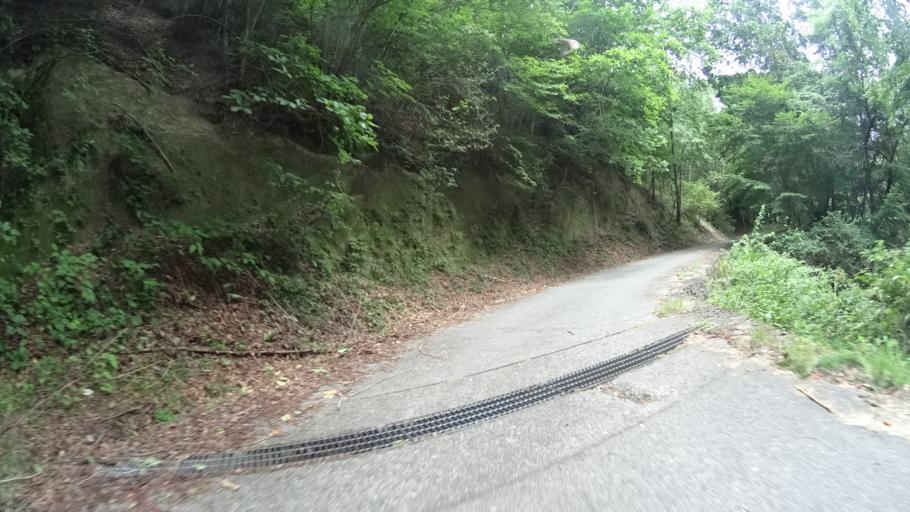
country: JP
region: Yamanashi
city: Kofu-shi
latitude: 35.8262
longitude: 138.5927
